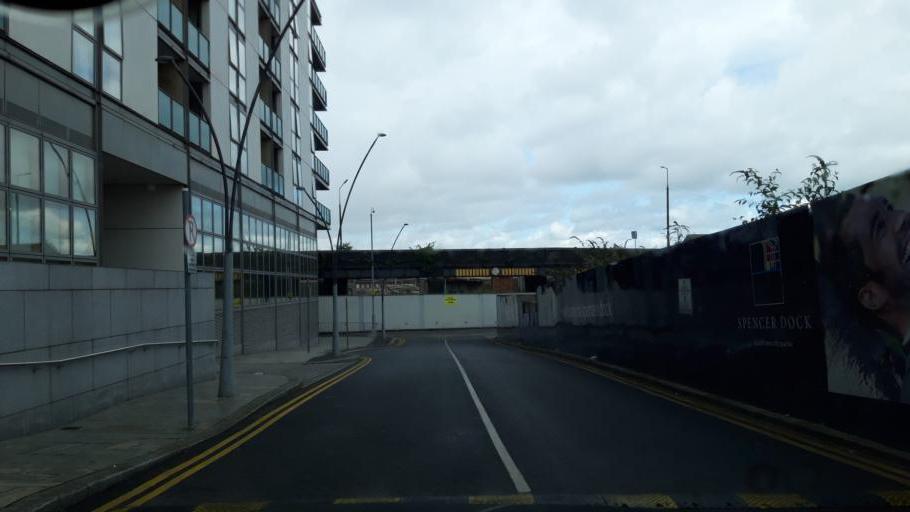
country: IE
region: Leinster
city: Ringsend
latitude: 53.3497
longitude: -6.2376
